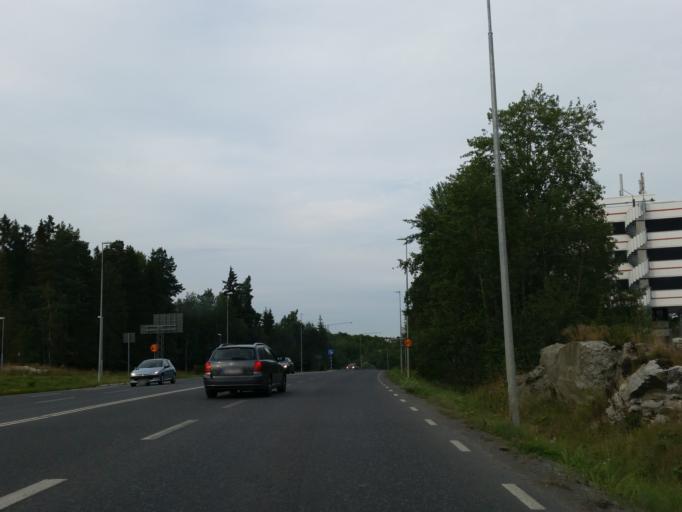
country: SE
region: Stockholm
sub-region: Jarfalla Kommun
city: Jakobsberg
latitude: 59.4089
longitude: 17.8464
